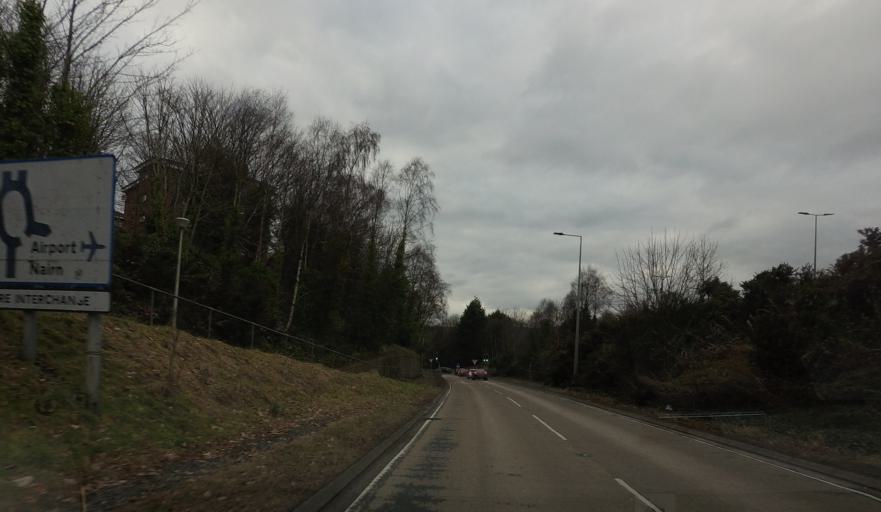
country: GB
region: Scotland
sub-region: Highland
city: Inverness
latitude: 57.4806
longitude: -4.1911
